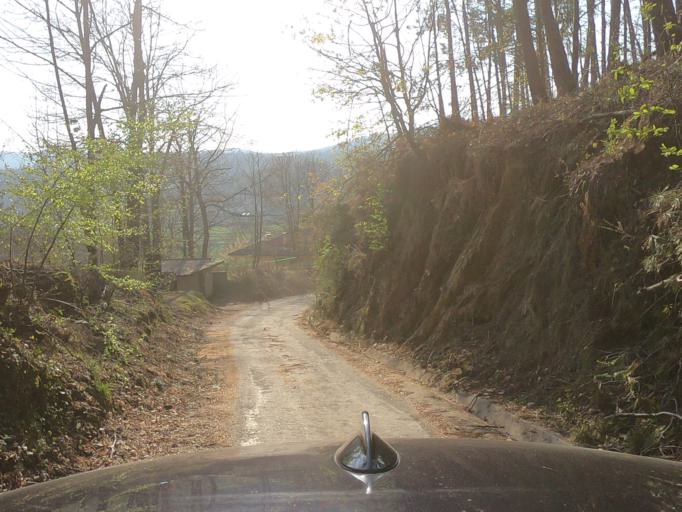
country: PT
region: Vila Real
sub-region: Vila Real
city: Vila Real
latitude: 41.3143
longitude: -7.8526
